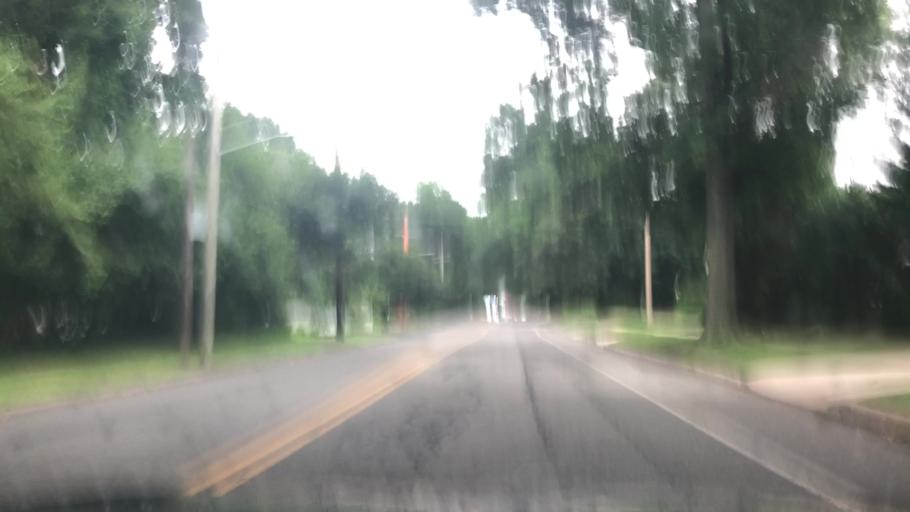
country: US
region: New York
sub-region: Nassau County
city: Garden City
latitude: 40.7115
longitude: -73.6361
